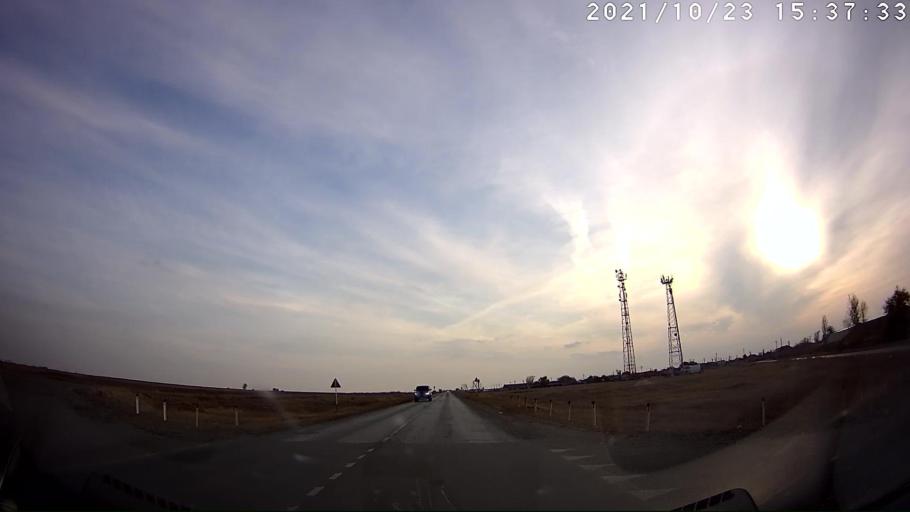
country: RU
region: Volgograd
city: Bereslavka
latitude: 48.1433
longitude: 44.1230
